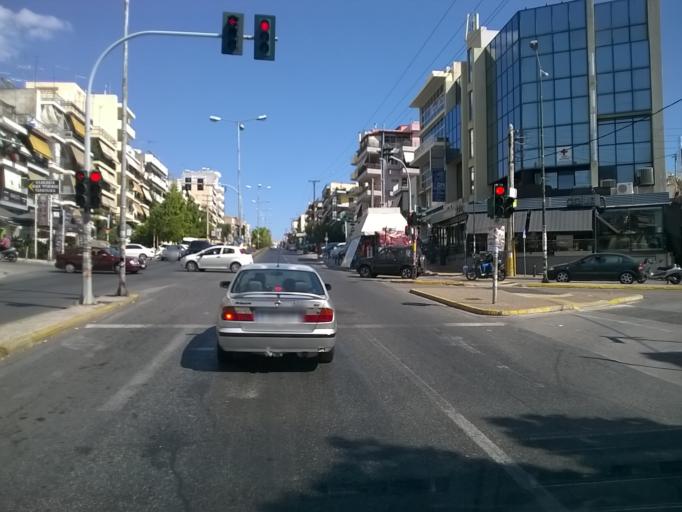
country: GR
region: Attica
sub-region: Nomos Piraios
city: Keratsini
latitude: 37.9708
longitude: 23.6211
